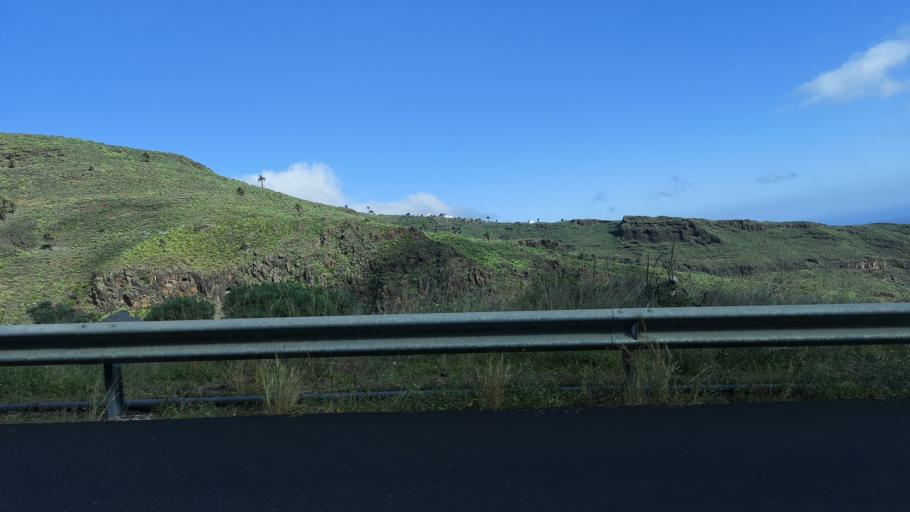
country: ES
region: Canary Islands
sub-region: Provincia de Santa Cruz de Tenerife
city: Alajero
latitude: 28.0684
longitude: -17.2065
